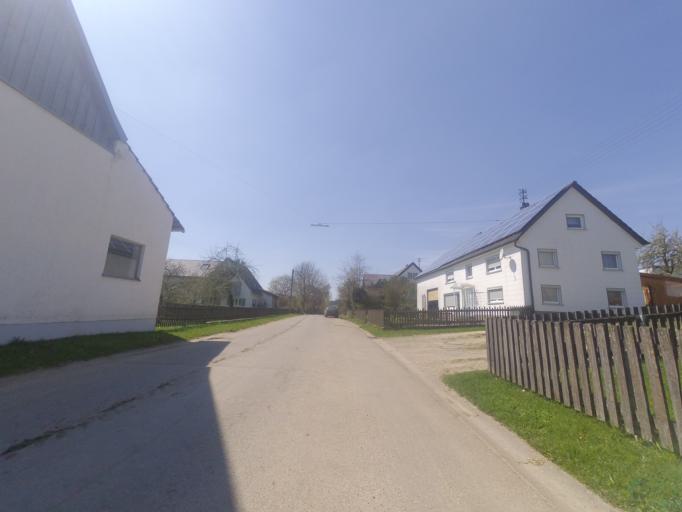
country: DE
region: Bavaria
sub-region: Swabia
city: Roggenburg
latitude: 48.2852
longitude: 10.2117
